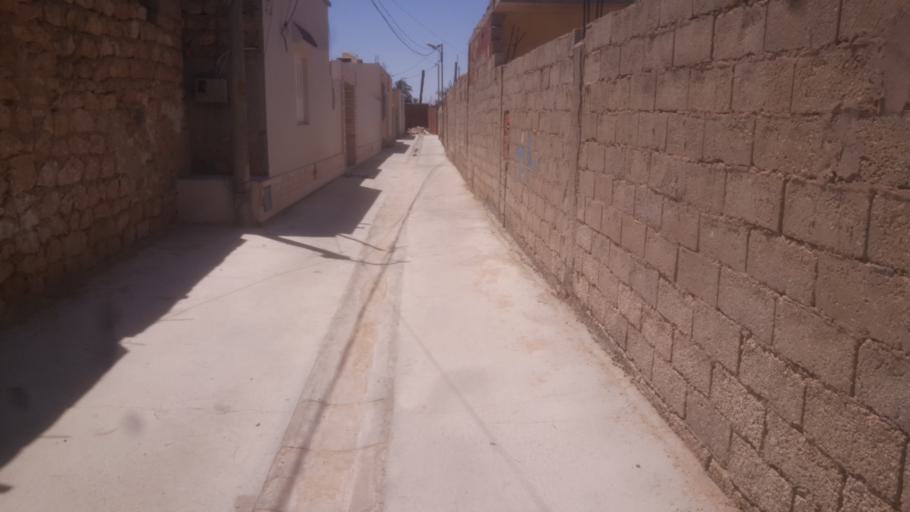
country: TN
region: Qabis
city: Gabes
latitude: 33.9439
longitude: 10.0719
